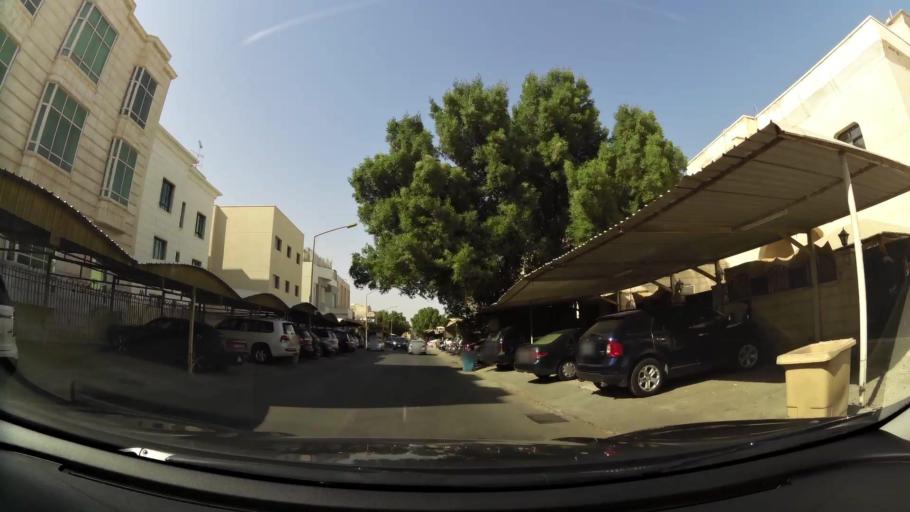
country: KW
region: Muhafazat Hawalli
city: Salwa
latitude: 29.2841
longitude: 48.0772
